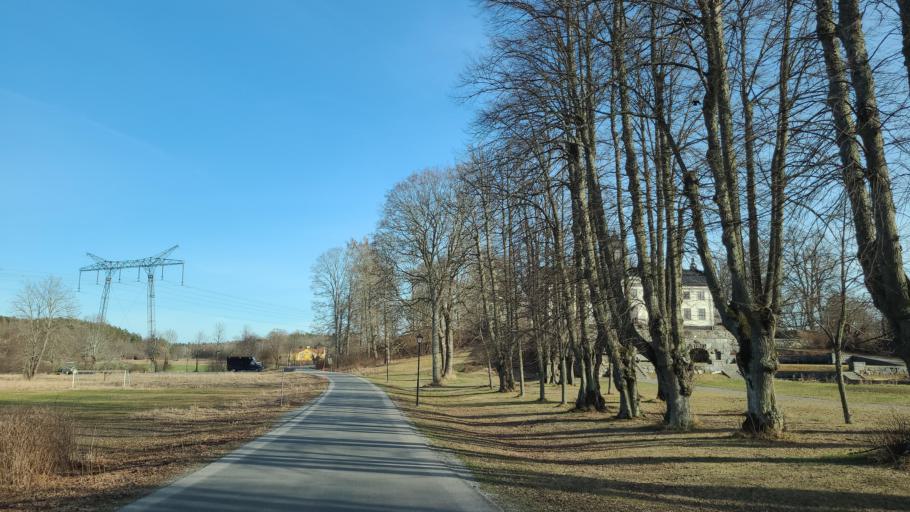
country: SE
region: Stockholm
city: Stenhamra
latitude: 59.2846
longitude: 17.6618
